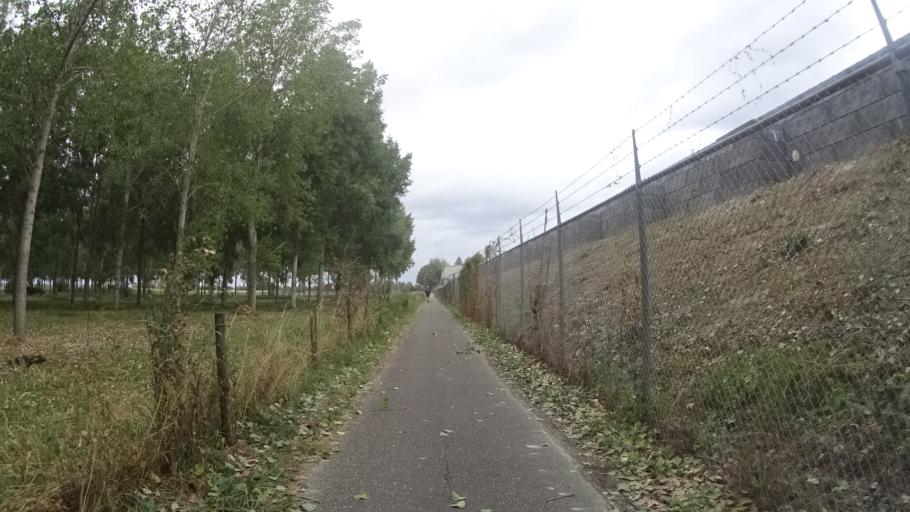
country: NL
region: Limburg
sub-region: Gemeente Maastricht
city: Maastricht
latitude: 50.8846
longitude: 5.7039
